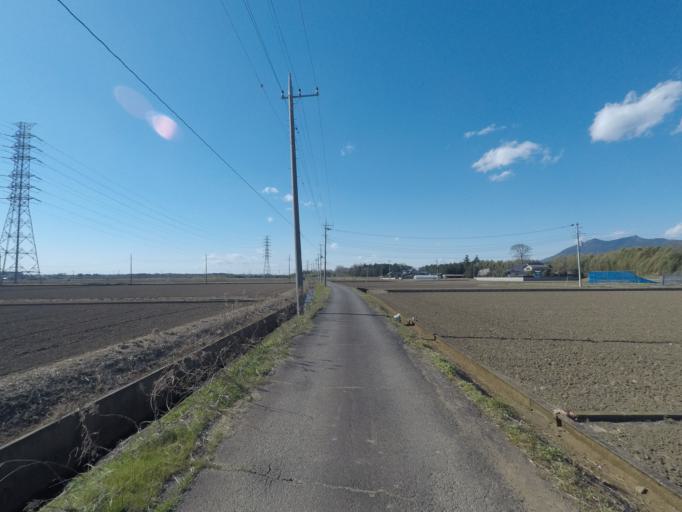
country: JP
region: Ibaraki
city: Tsukuba
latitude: 36.1399
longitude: 140.1166
